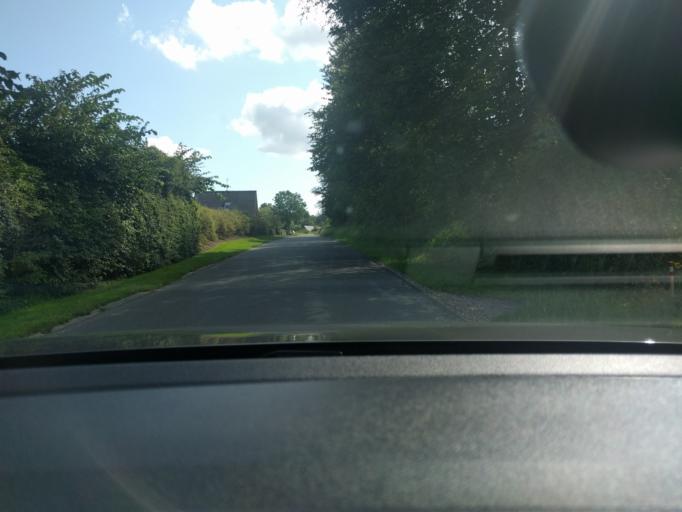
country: DK
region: Central Jutland
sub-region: Viborg Kommune
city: Viborg
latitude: 56.5253
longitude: 9.3695
